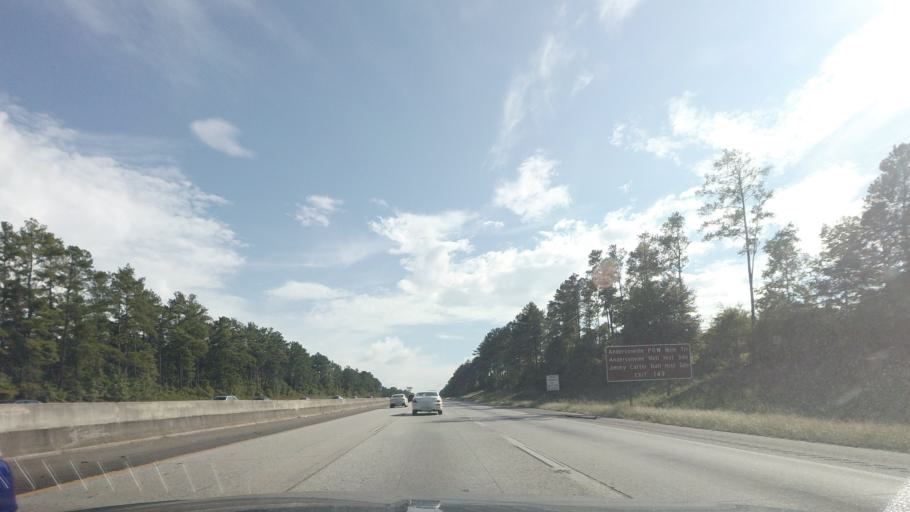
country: US
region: Georgia
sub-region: Peach County
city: Byron
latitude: 32.6914
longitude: -83.7389
